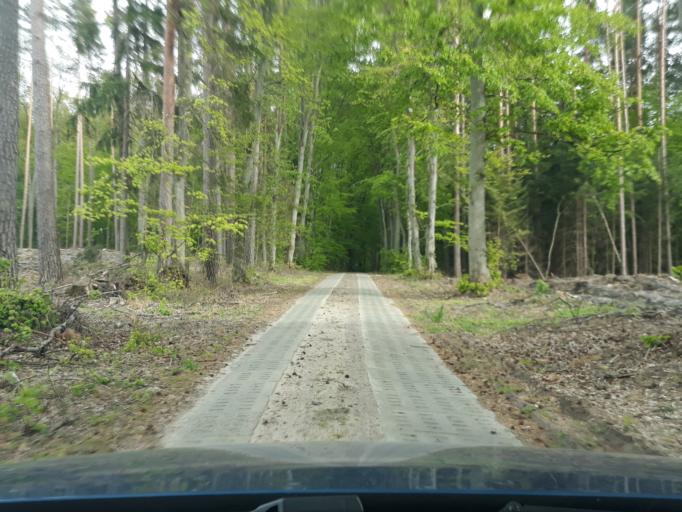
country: PL
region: Pomeranian Voivodeship
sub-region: Powiat czluchowski
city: Czluchow
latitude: 53.7540
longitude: 17.3423
